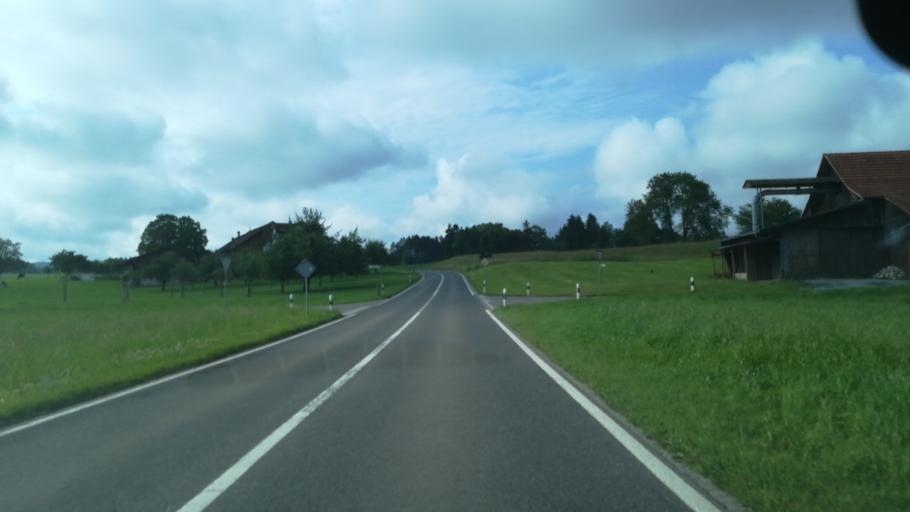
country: CH
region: Saint Gallen
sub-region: Wahlkreis St. Gallen
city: Andwil
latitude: 47.4598
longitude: 9.2489
